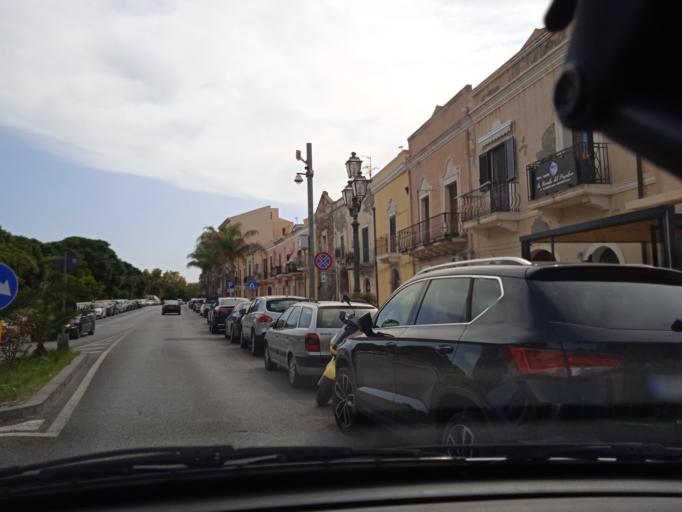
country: IT
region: Sicily
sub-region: Messina
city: Milazzo
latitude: 38.2302
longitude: 15.2474
